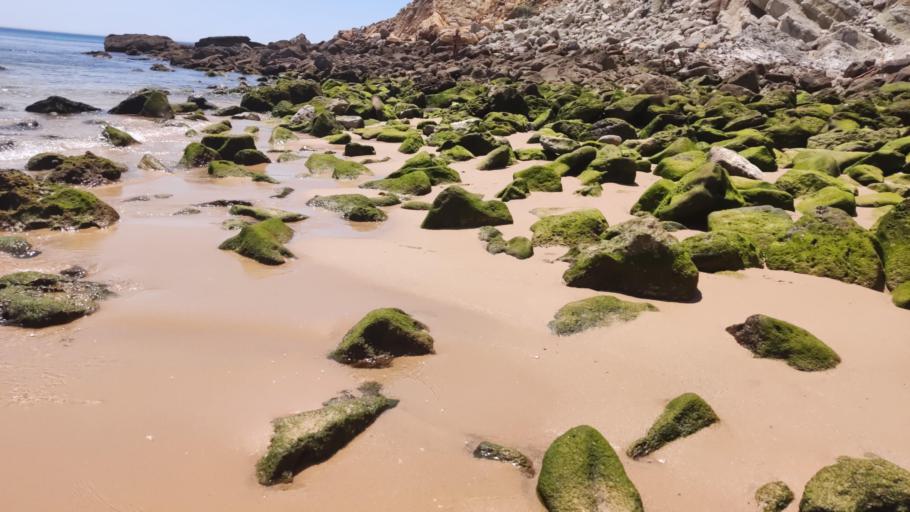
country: PT
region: Faro
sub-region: Lagos
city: Lagos
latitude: 37.0703
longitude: -8.7774
